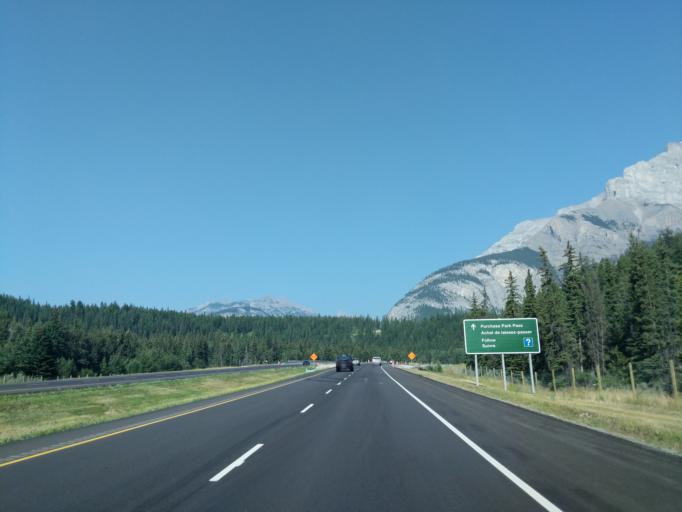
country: CA
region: Alberta
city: Banff
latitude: 51.2020
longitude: -115.5142
